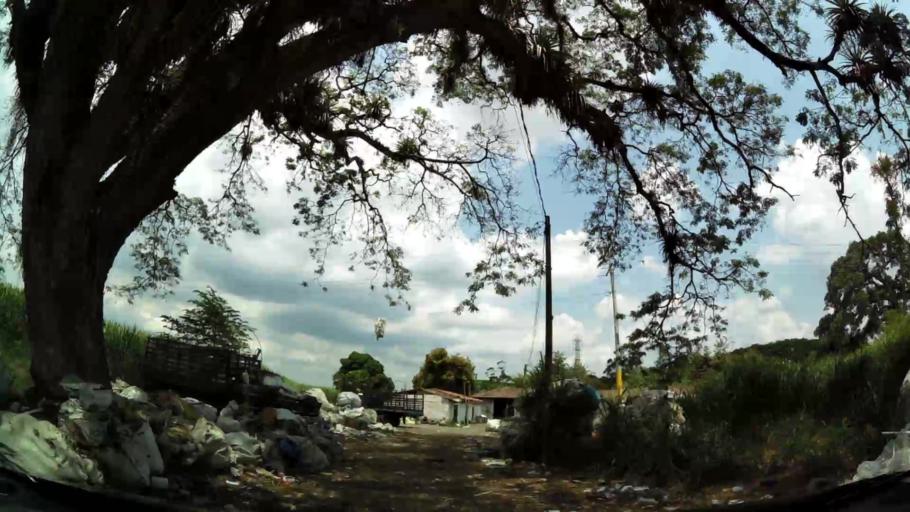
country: CO
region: Valle del Cauca
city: Cali
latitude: 3.4548
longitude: -76.4728
